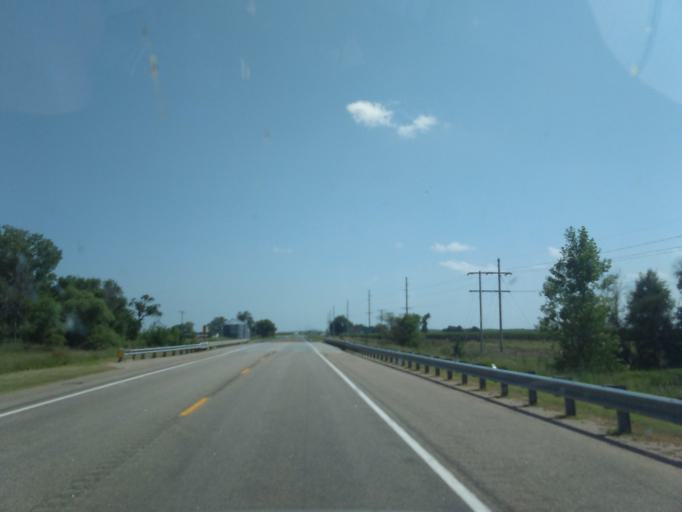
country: US
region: Nebraska
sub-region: Phelps County
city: Holdrege
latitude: 40.6659
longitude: -99.3805
